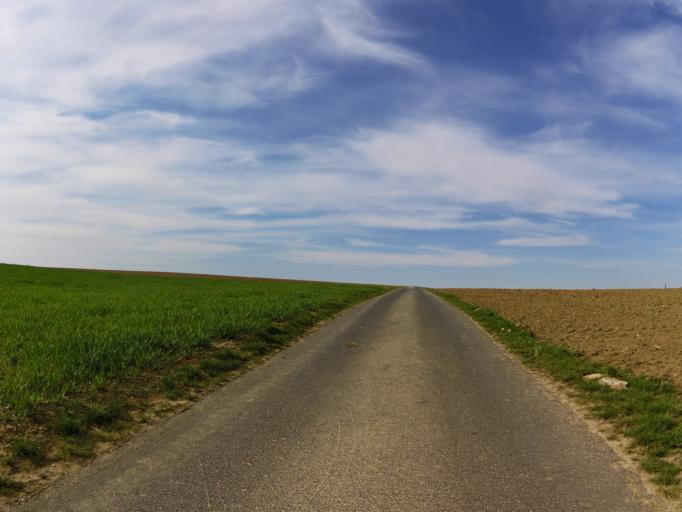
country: DE
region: Bavaria
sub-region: Regierungsbezirk Unterfranken
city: Kurnach
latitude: 49.8649
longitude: 10.0243
